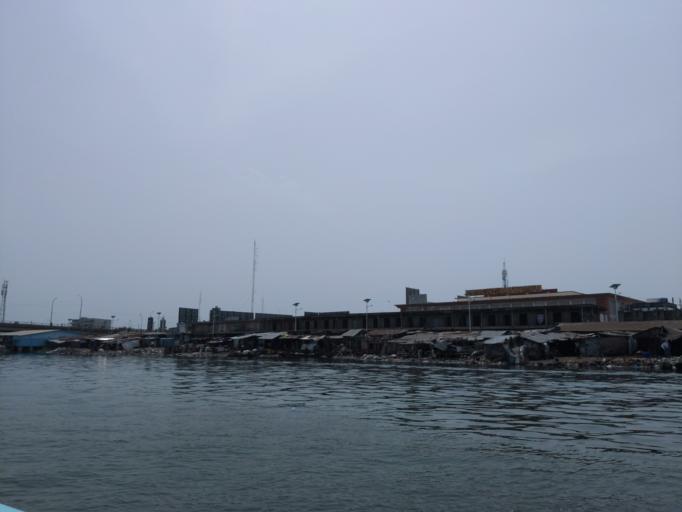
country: BJ
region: Littoral
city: Cotonou
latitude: 6.3728
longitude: 2.4362
